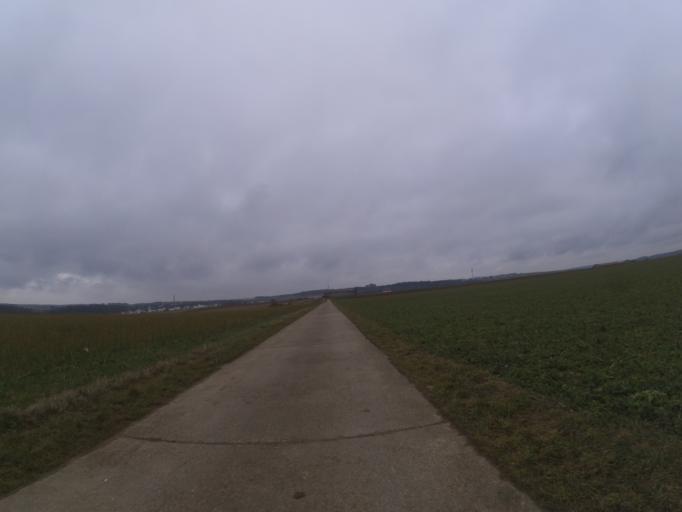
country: DE
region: Baden-Wuerttemberg
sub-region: Tuebingen Region
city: Dornstadt
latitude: 48.4414
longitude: 9.9286
